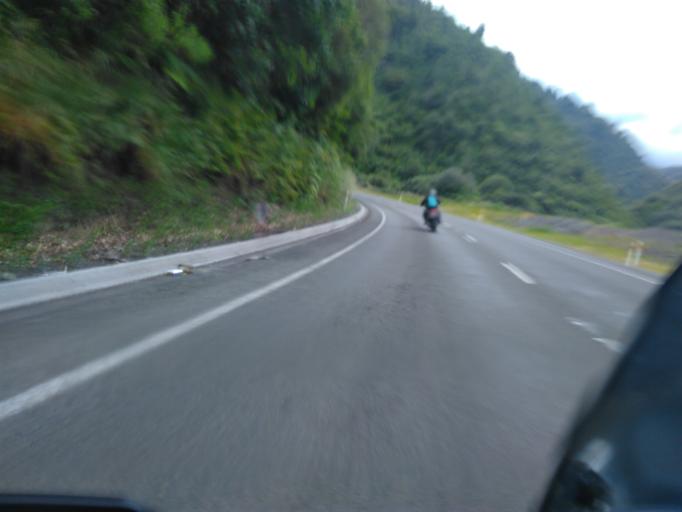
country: NZ
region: Bay of Plenty
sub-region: Opotiki District
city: Opotiki
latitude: -38.3179
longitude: 177.3954
